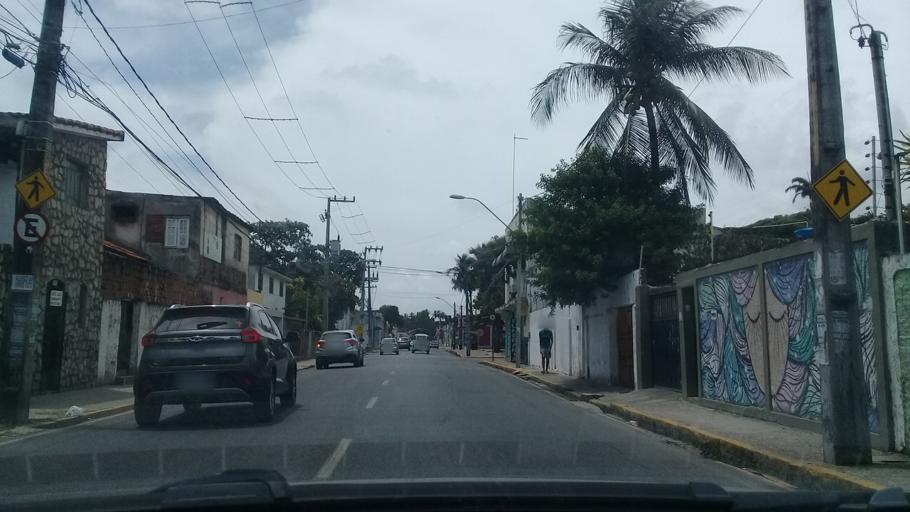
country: BR
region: Pernambuco
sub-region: Olinda
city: Olinda
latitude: -8.0129
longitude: -34.8440
